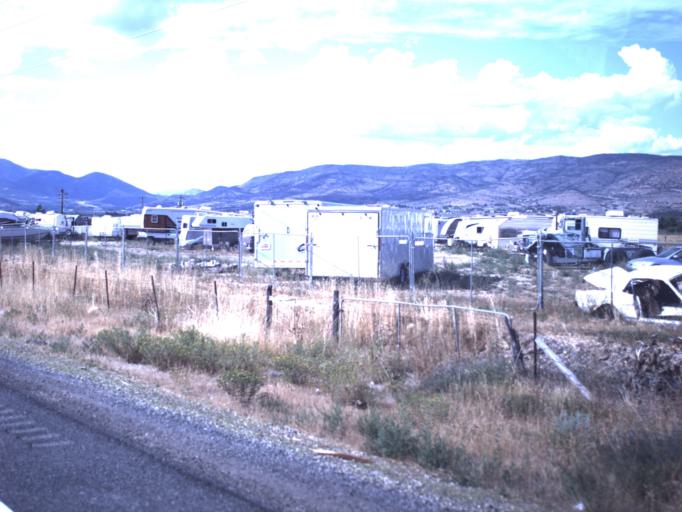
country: US
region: Utah
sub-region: Wasatch County
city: Heber
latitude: 40.4803
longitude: -111.4004
